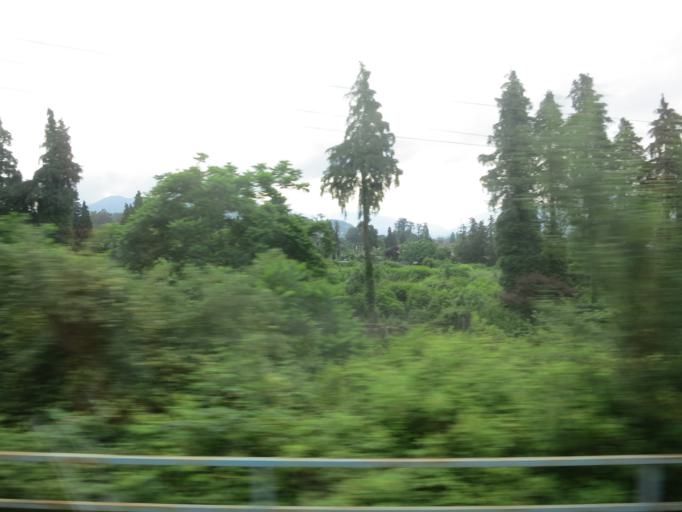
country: GE
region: Ajaria
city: Makhinjauri
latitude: 41.7202
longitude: 41.7288
